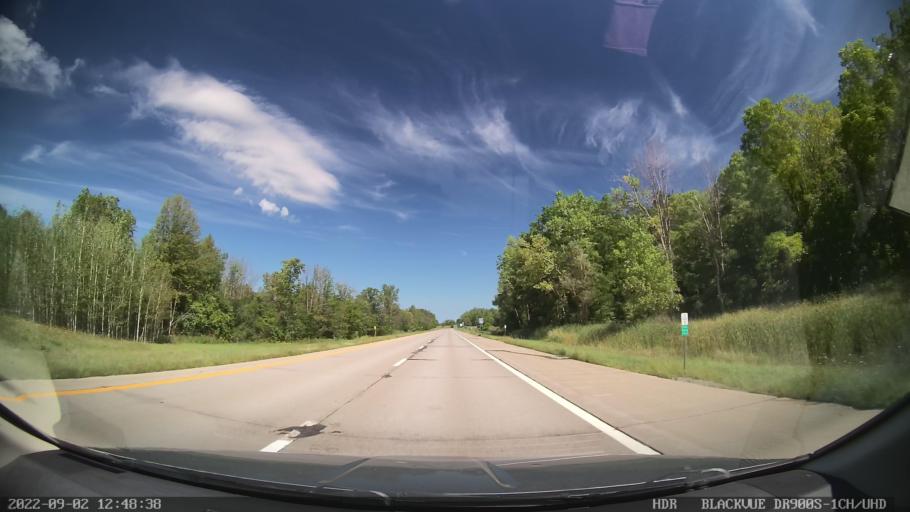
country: US
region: New York
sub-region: Livingston County
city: Livonia
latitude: 42.8364
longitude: -77.7334
